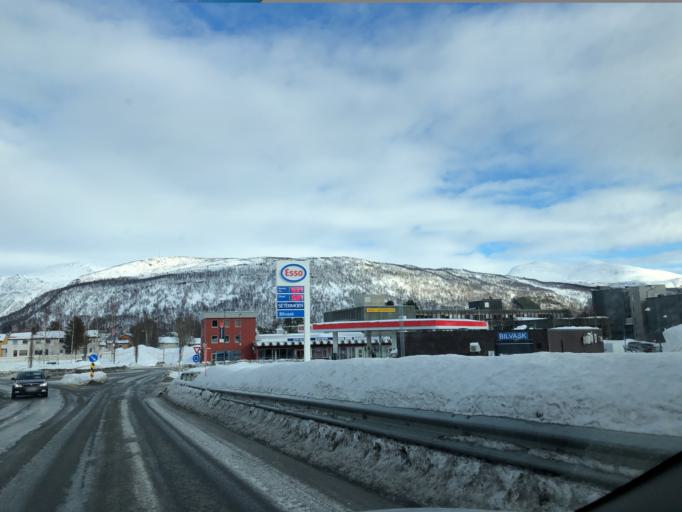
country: NO
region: Troms
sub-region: Bardu
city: Setermoen
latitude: 68.8605
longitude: 18.3465
